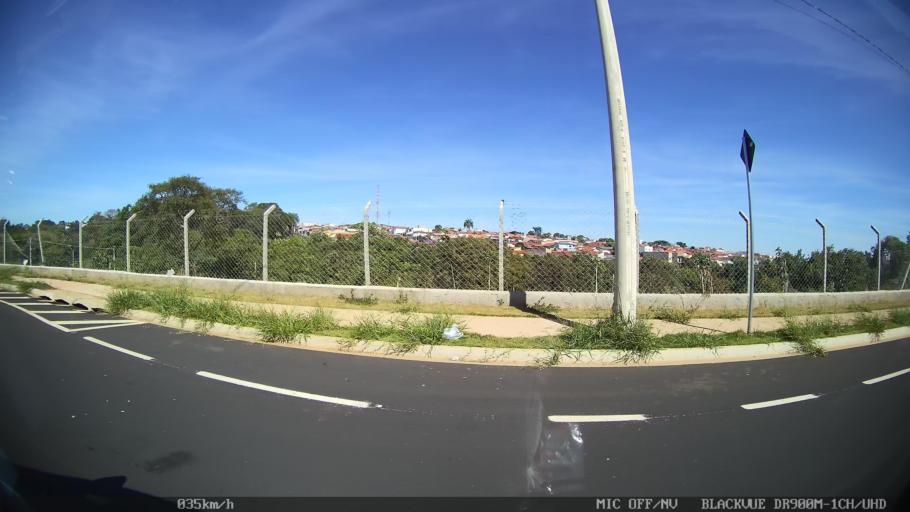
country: BR
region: Sao Paulo
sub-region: Franca
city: Franca
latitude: -20.5561
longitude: -47.3665
